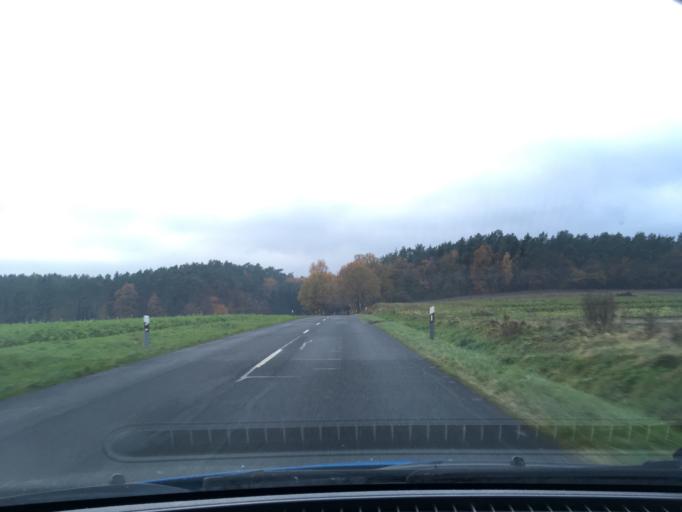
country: DE
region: Lower Saxony
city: Eyendorf
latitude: 53.1756
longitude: 10.1734
